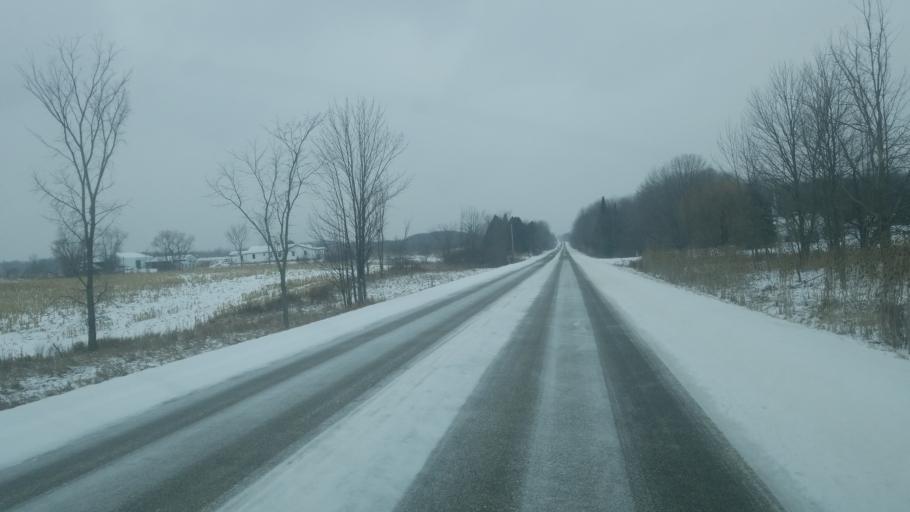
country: US
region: Michigan
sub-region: Osceola County
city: Evart
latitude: 44.1025
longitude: -85.1900
